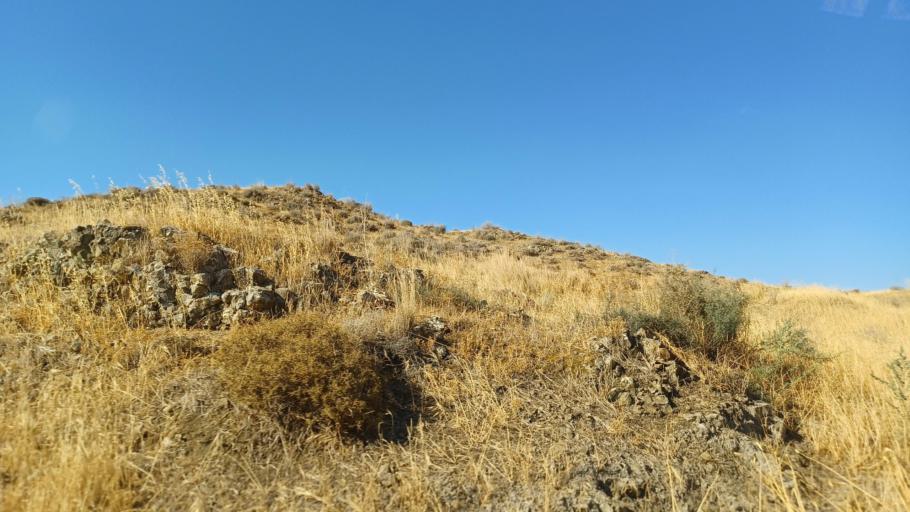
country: CY
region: Larnaka
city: Troulloi
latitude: 35.0045
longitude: 33.5913
